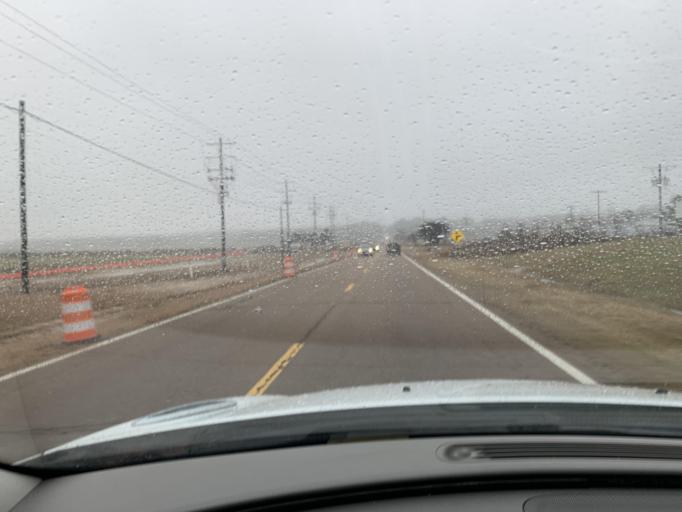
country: US
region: Mississippi
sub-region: De Soto County
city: Hernando
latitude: 34.8653
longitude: -89.9954
